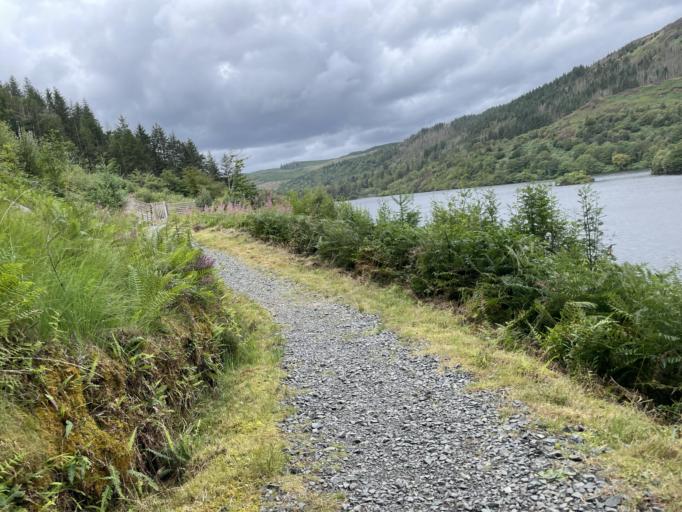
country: GB
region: Scotland
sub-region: Dumfries and Galloway
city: Newton Stewart
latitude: 55.0868
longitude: -4.4797
